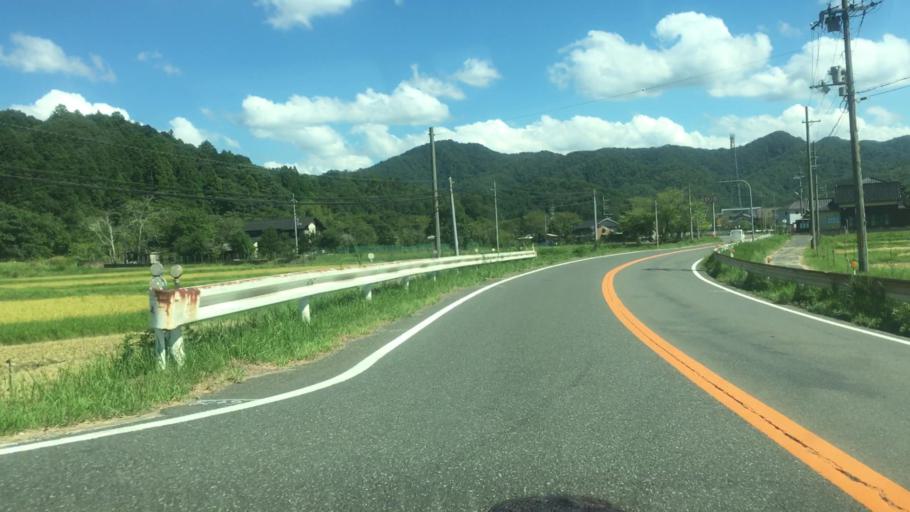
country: JP
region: Hyogo
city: Toyooka
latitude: 35.5802
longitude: 134.9696
